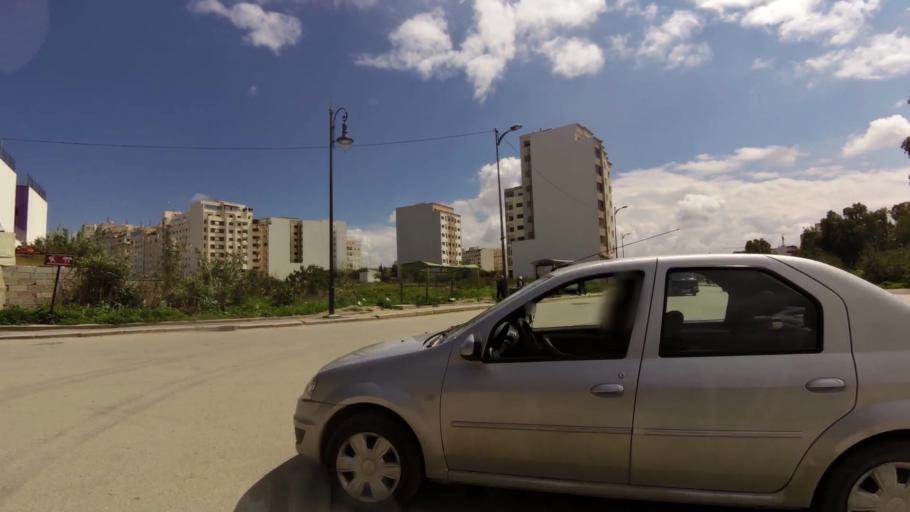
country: MA
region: Tanger-Tetouan
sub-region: Tanger-Assilah
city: Tangier
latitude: 35.7669
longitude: -5.8473
